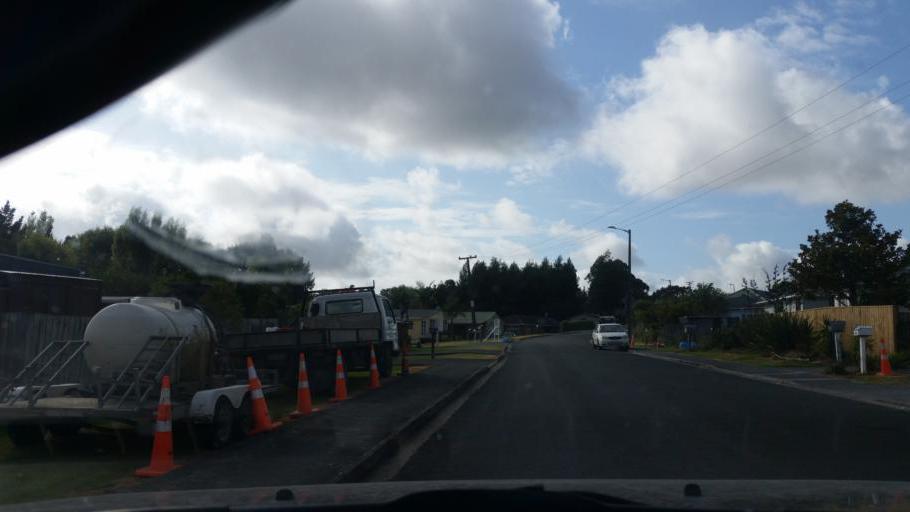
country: NZ
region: Auckland
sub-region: Auckland
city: Wellsford
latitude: -36.1660
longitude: 174.4456
